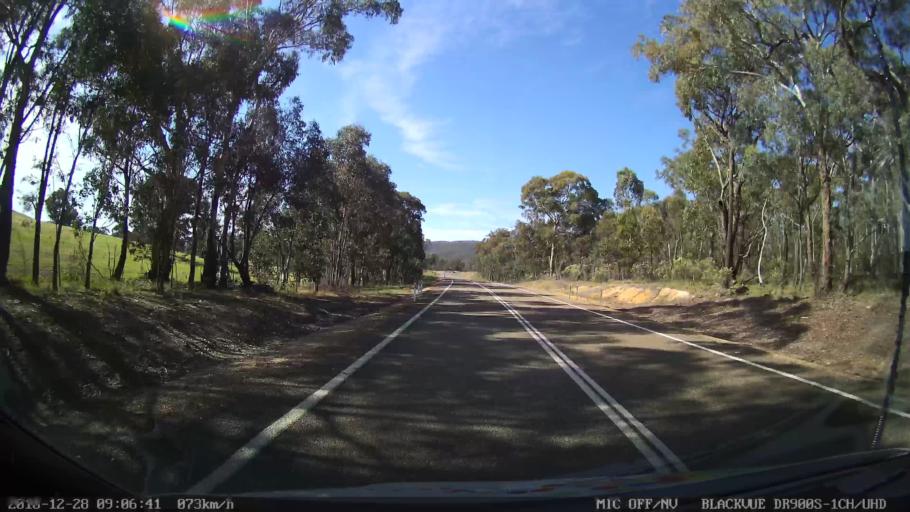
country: AU
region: New South Wales
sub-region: Upper Lachlan Shire
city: Crookwell
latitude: -34.1986
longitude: 149.3462
